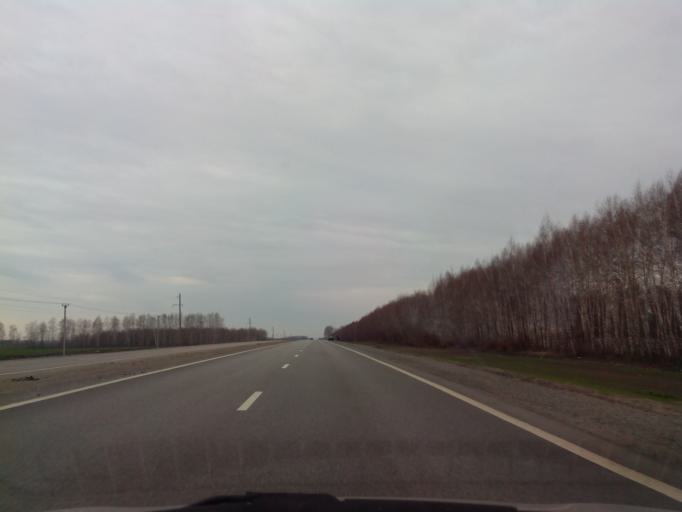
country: RU
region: Tambov
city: Zavoronezhskoye
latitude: 52.8801
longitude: 40.7385
